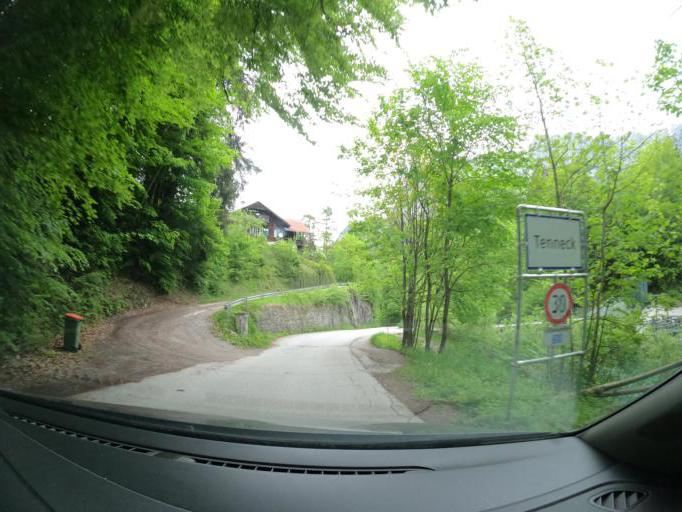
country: AT
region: Salzburg
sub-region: Politischer Bezirk Sankt Johann im Pongau
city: Werfen
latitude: 47.4912
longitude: 13.1689
